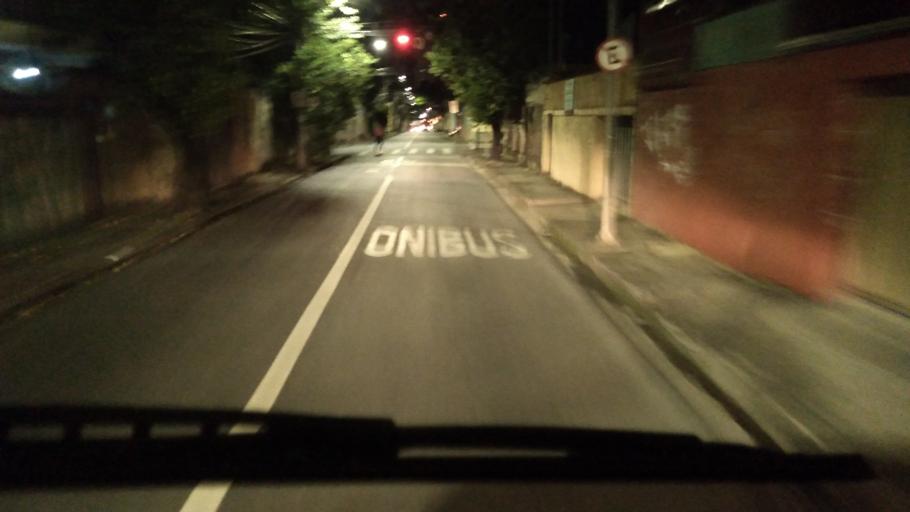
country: BR
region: Minas Gerais
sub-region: Belo Horizonte
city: Belo Horizonte
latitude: -19.9129
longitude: -43.9680
